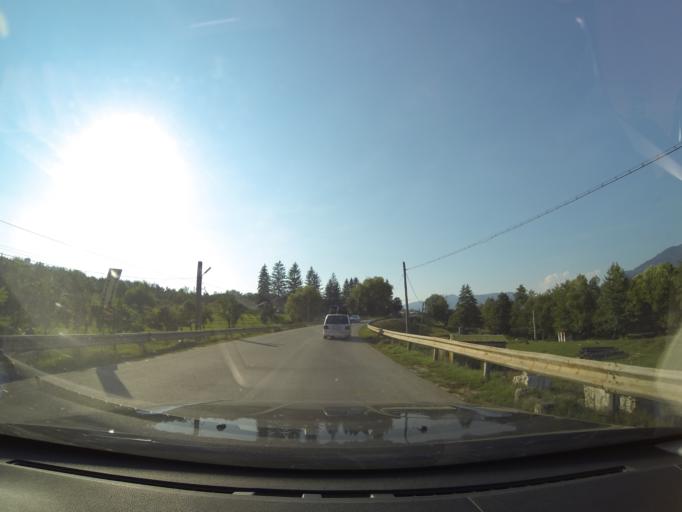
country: RO
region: Arges
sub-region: Comuna Corbeni
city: Corbeni
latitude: 45.3070
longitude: 24.6517
